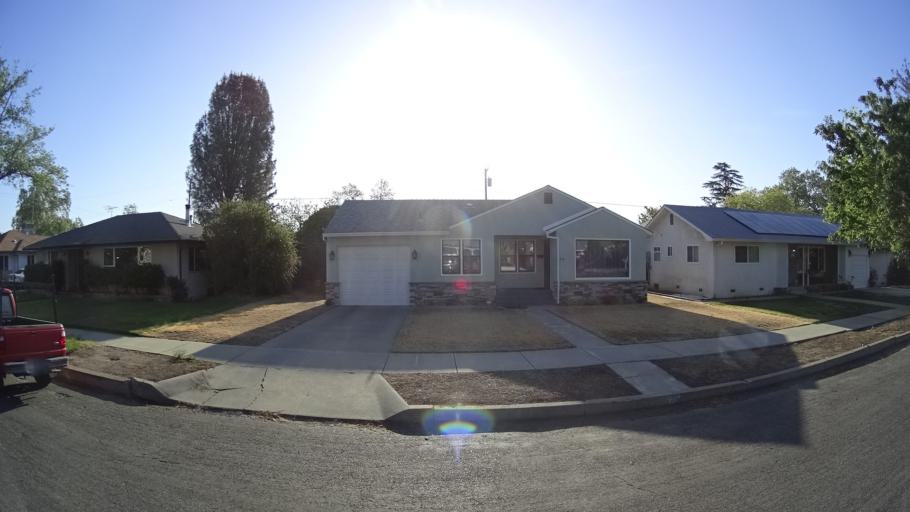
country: US
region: California
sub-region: Glenn County
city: Orland
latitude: 39.7490
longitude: -122.1902
